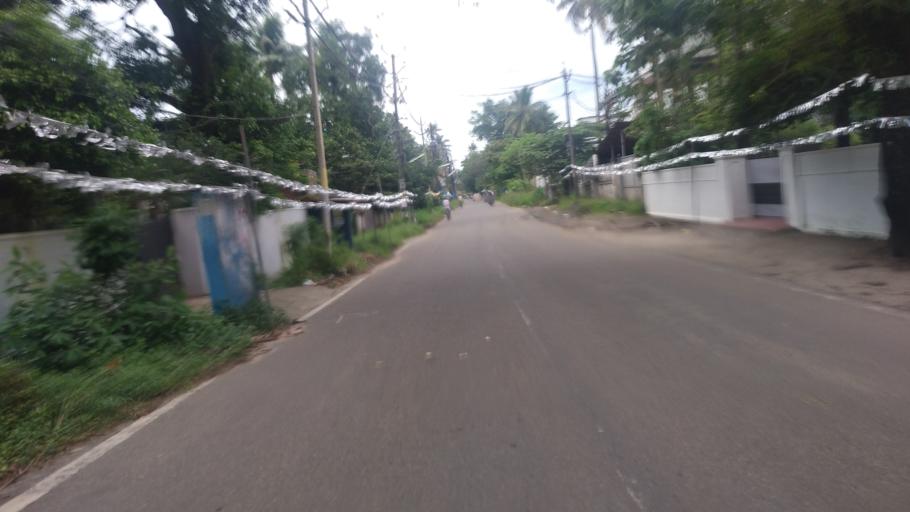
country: IN
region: Kerala
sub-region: Ernakulam
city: Cochin
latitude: 9.8972
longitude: 76.2581
